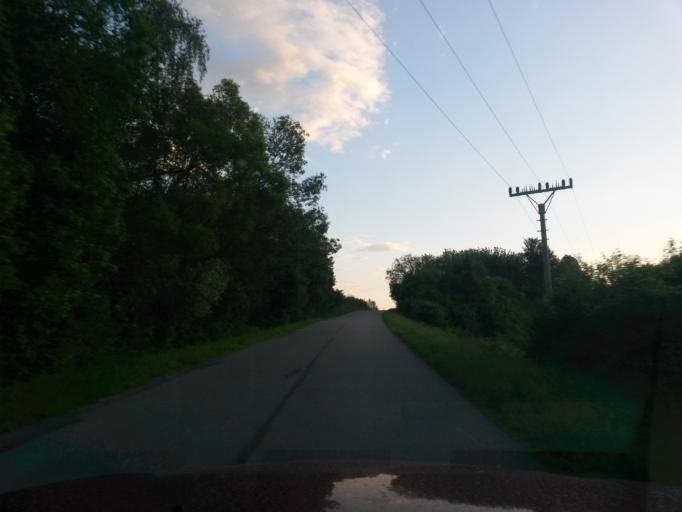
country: UA
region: Zakarpattia
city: Kamianytsia
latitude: 48.8173
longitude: 22.3461
